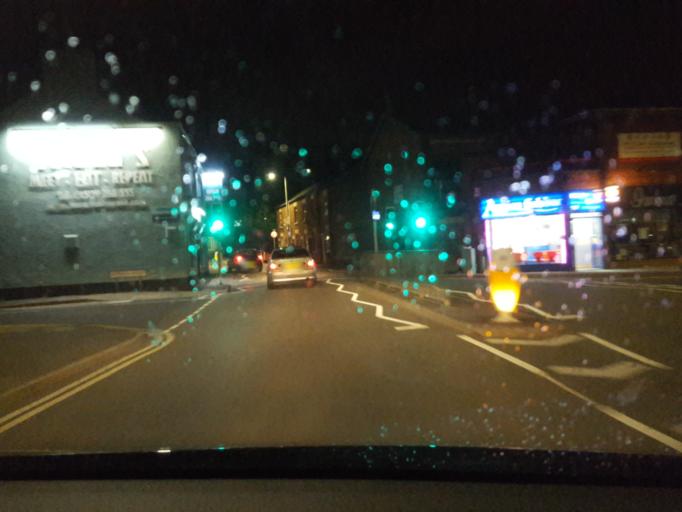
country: GB
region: England
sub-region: Leicestershire
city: Loughborough
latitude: 52.7685
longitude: -1.2069
